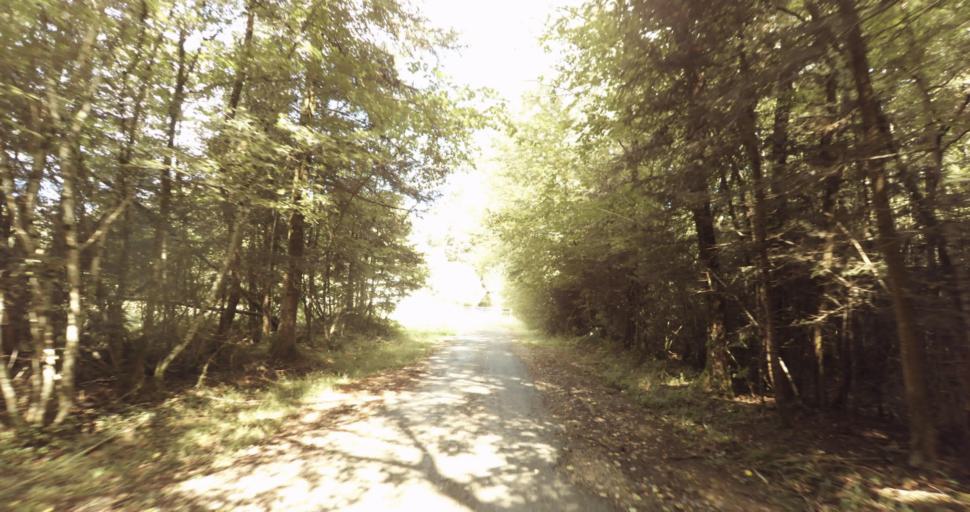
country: FR
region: Lower Normandy
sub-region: Departement de l'Orne
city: Gace
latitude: 48.7826
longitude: 0.3236
